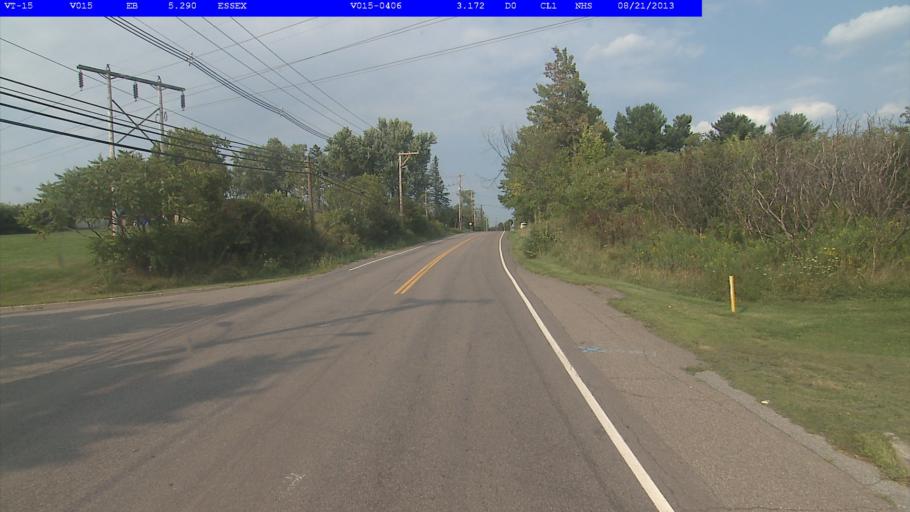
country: US
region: Vermont
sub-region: Chittenden County
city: Essex Junction
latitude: 44.5001
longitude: -73.0975
